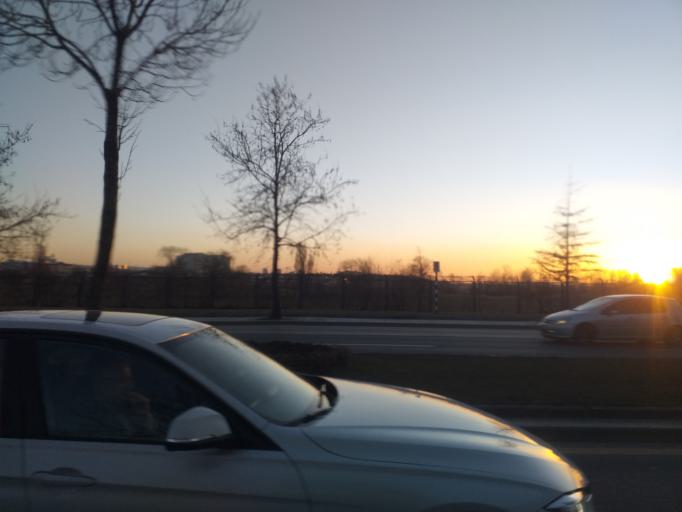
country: TR
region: Ankara
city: Ankara
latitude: 39.9508
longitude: 32.8244
